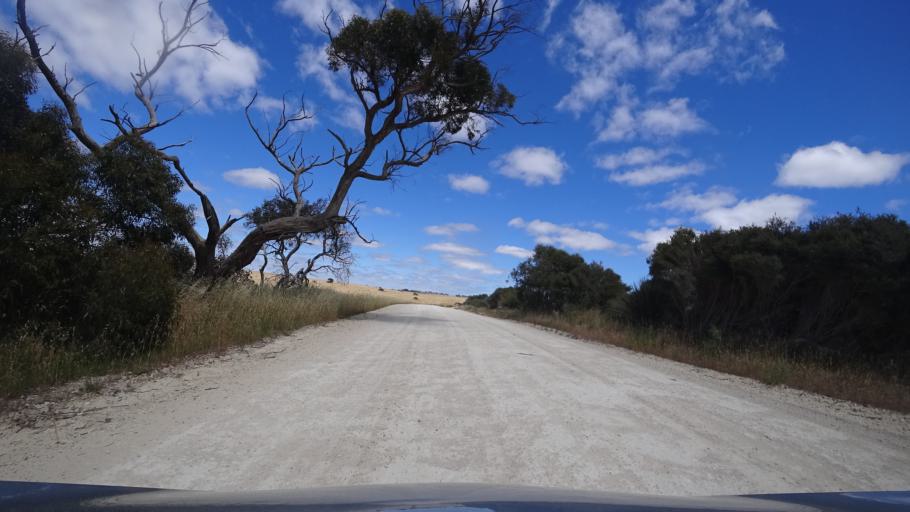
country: AU
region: South Australia
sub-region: Kangaroo Island
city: Kingscote
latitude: -35.6445
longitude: 137.3557
